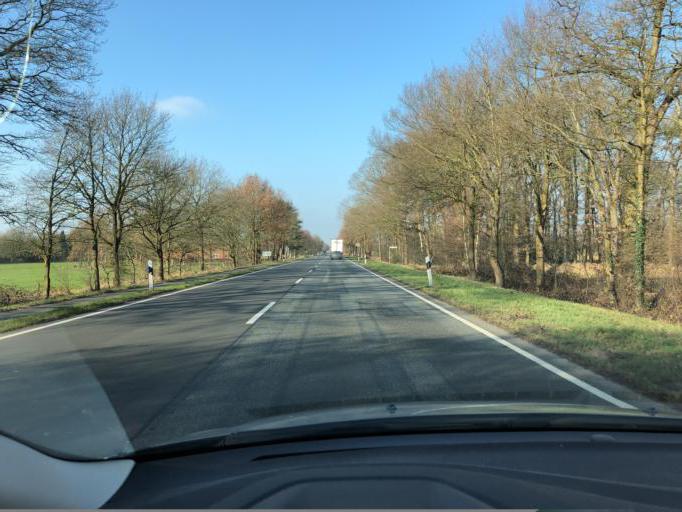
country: DE
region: Lower Saxony
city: Apen
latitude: 53.2951
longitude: 7.8324
